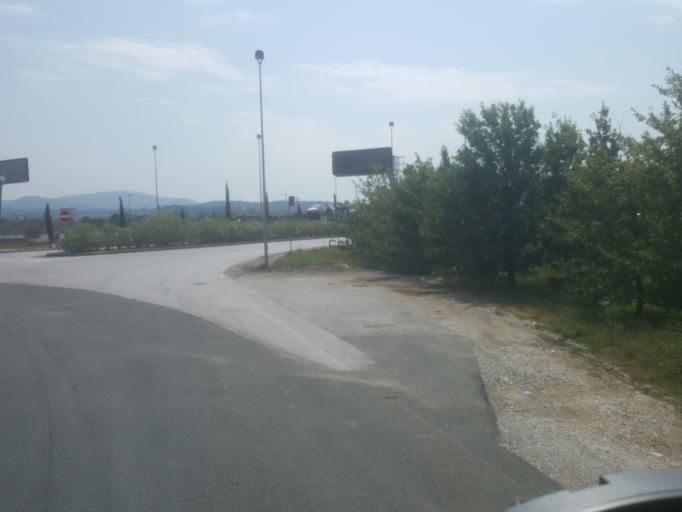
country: IT
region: Tuscany
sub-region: Provincia di Livorno
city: Guasticce
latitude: 43.6070
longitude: 10.4071
